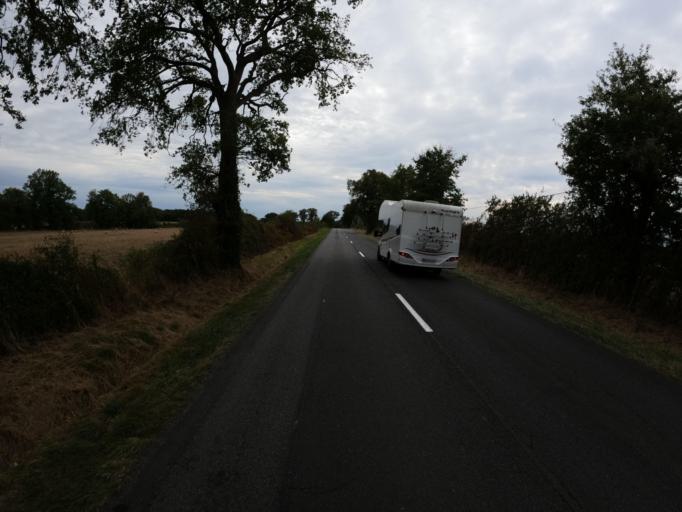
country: FR
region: Poitou-Charentes
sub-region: Departement de la Vienne
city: Saulge
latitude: 46.3384
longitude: 0.8233
